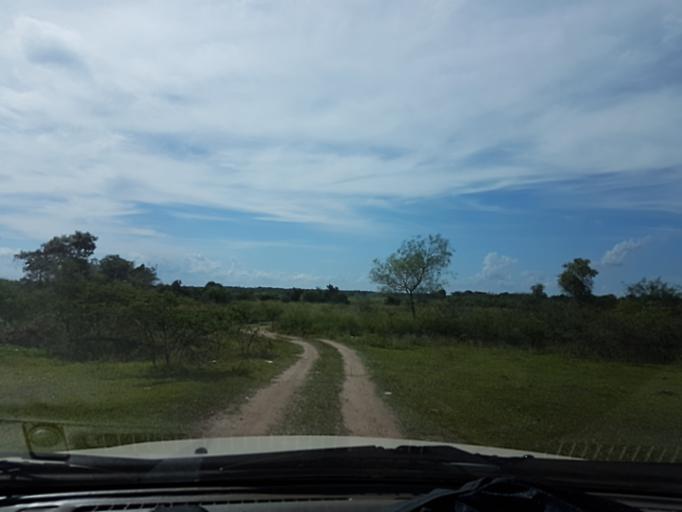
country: PY
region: Cordillera
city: Arroyos y Esteros
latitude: -24.9738
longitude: -57.1932
